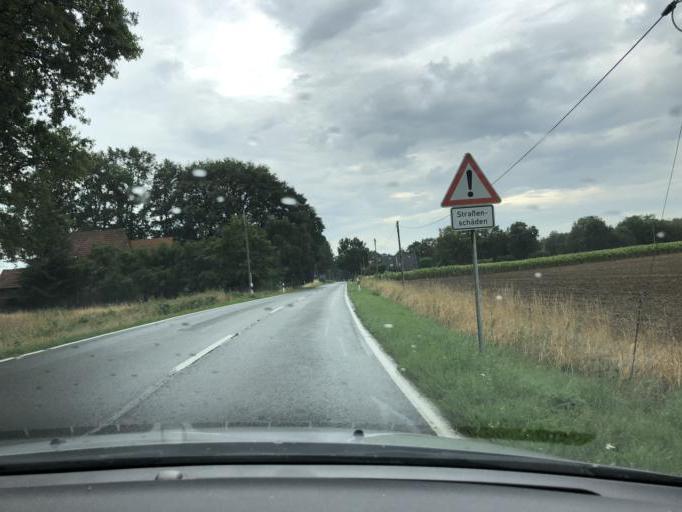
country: DE
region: North Rhine-Westphalia
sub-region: Regierungsbezirk Dusseldorf
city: Schermbeck
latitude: 51.6411
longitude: 6.8972
